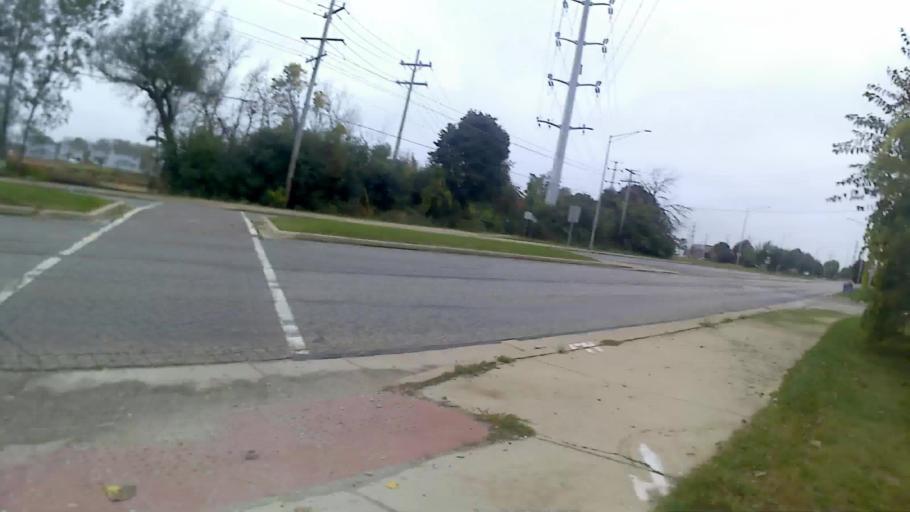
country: US
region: Illinois
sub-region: DuPage County
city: Warrenville
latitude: 41.7990
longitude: -88.2220
